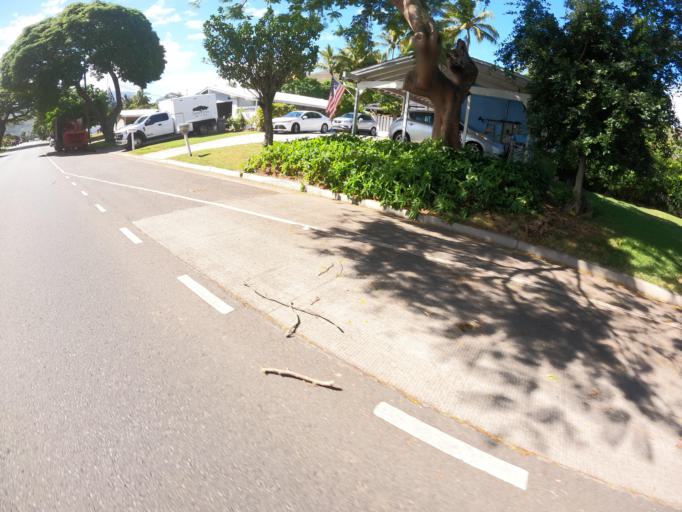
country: US
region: Hawaii
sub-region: Honolulu County
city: Kailua
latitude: 21.4113
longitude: -157.7538
